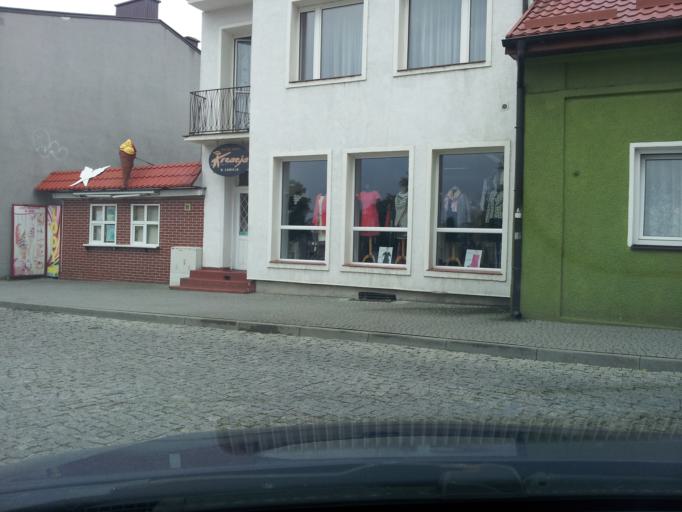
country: PL
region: Kujawsko-Pomorskie
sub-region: Powiat lipnowski
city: Lipno
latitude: 52.8456
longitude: 19.1819
